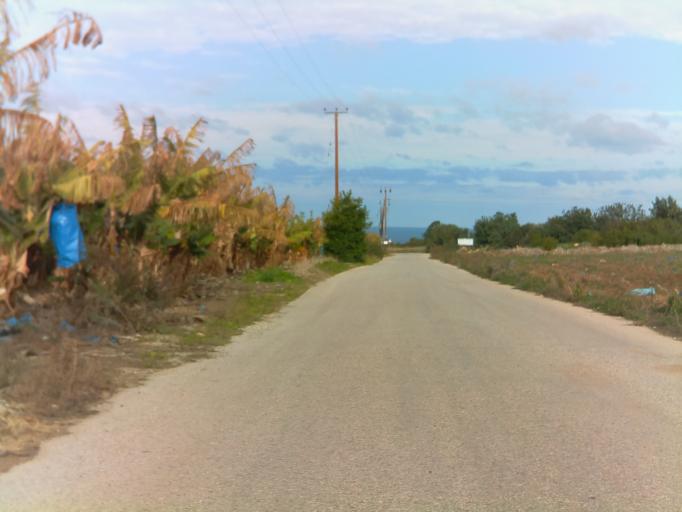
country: CY
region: Pafos
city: Pegeia
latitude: 34.9030
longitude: 32.3278
